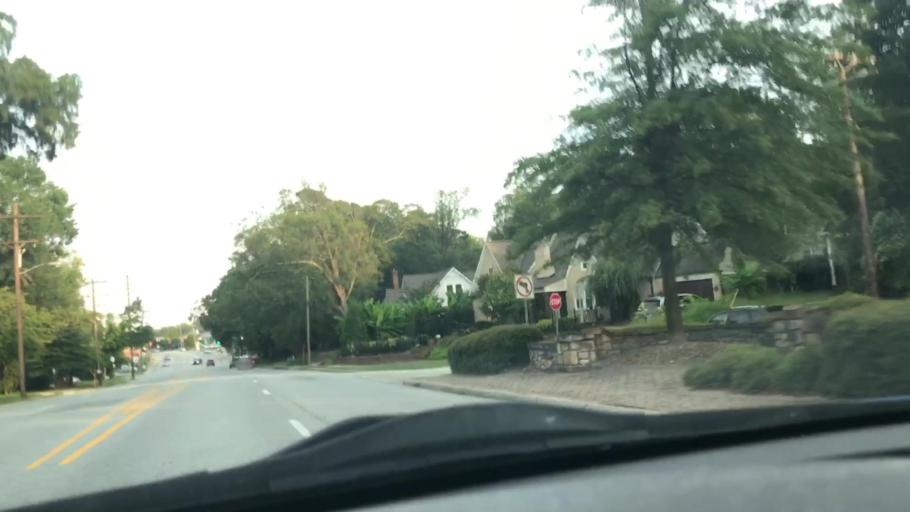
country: US
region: North Carolina
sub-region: Guilford County
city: Greensboro
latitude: 36.0771
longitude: -79.8191
